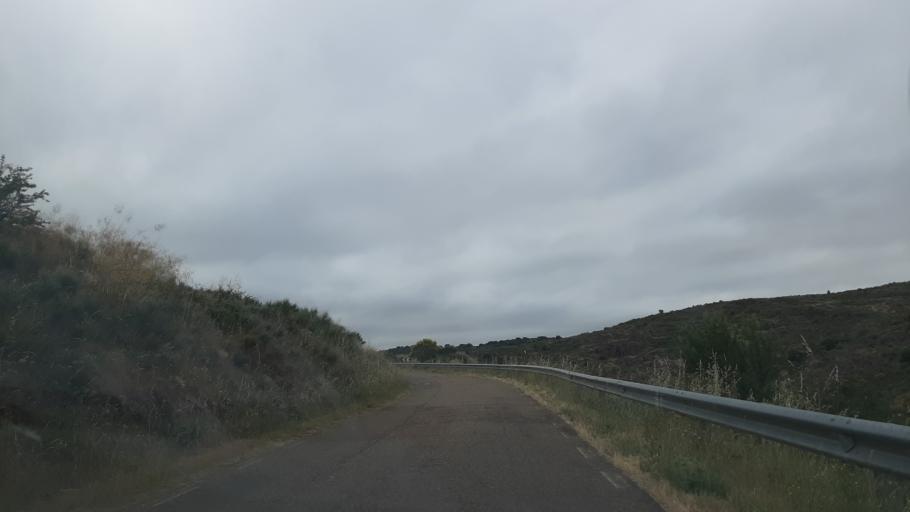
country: ES
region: Castille and Leon
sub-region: Provincia de Salamanca
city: Pastores
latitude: 40.5343
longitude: -6.4844
